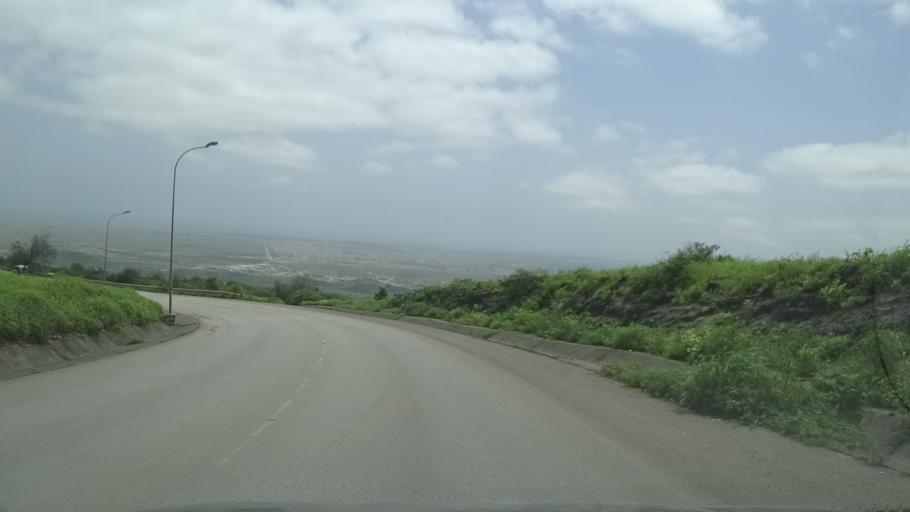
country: OM
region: Zufar
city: Salalah
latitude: 17.1543
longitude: 54.2173
